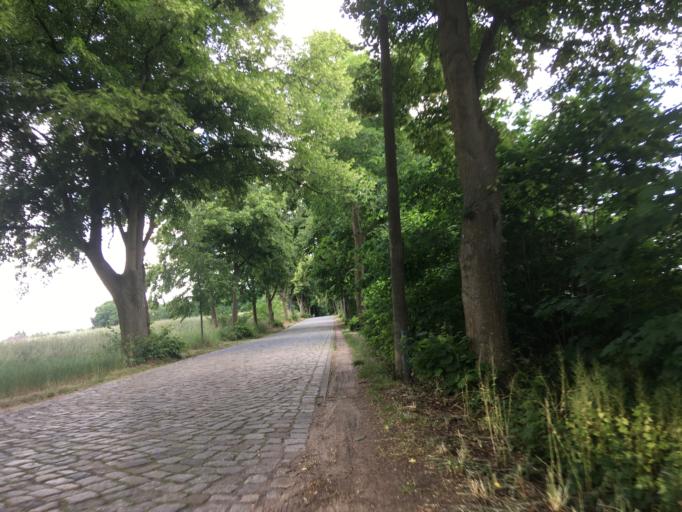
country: DE
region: Brandenburg
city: Muncheberg
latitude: 52.5286
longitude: 14.1023
